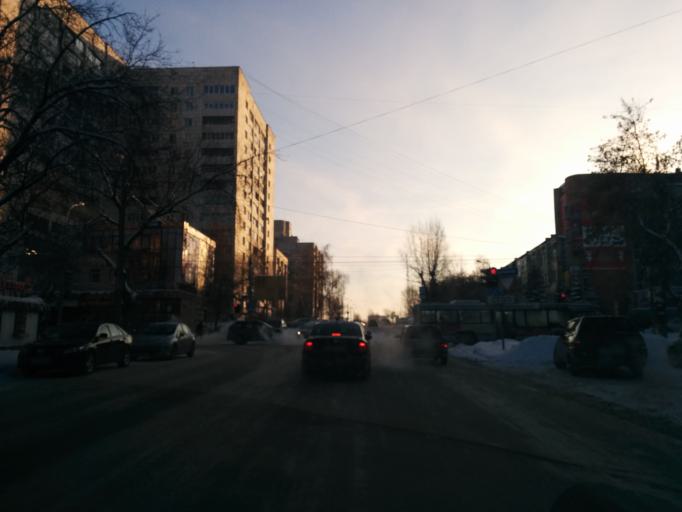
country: RU
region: Perm
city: Perm
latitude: 58.0047
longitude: 56.2141
